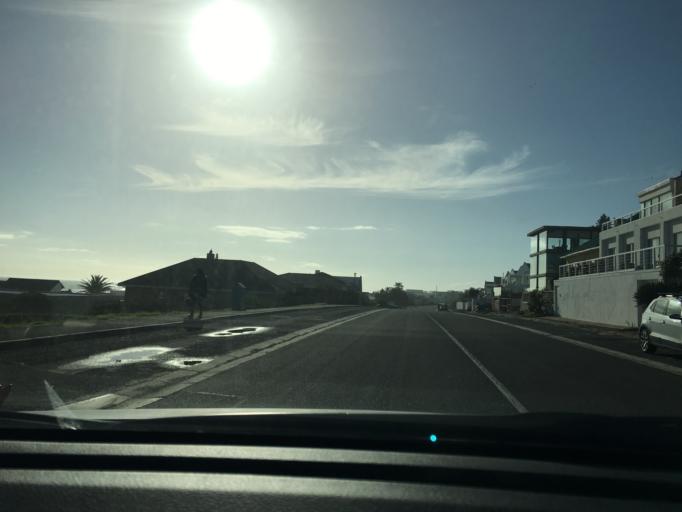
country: ZA
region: Western Cape
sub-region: City of Cape Town
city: Sunset Beach
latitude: -33.7961
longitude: 18.4596
